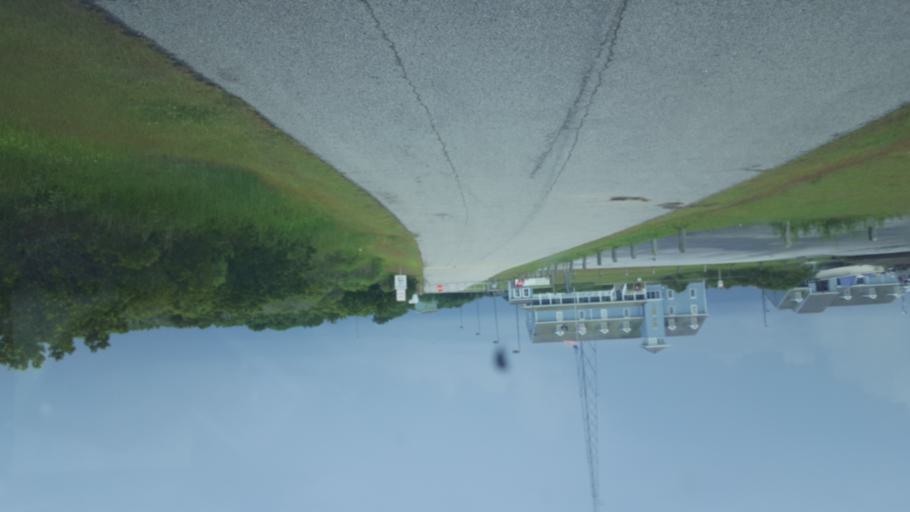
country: US
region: North Carolina
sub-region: Dare County
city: Wanchese
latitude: 35.7972
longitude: -75.5490
